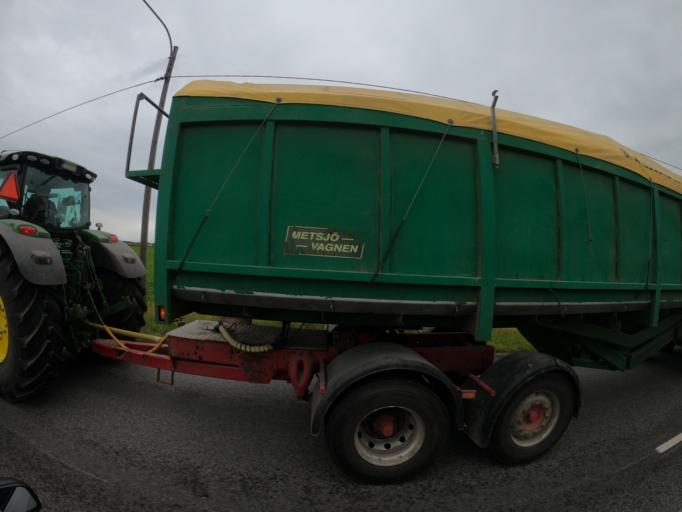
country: SE
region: Skane
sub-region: Lunds Kommun
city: Lund
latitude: 55.7352
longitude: 13.1991
